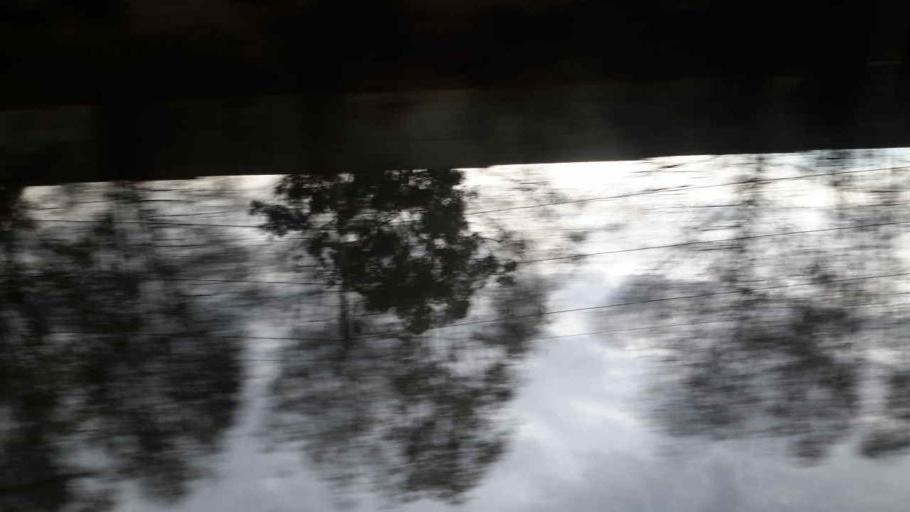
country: AU
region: New South Wales
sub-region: Camden
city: Narellan Vale
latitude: -34.0449
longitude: 150.7443
